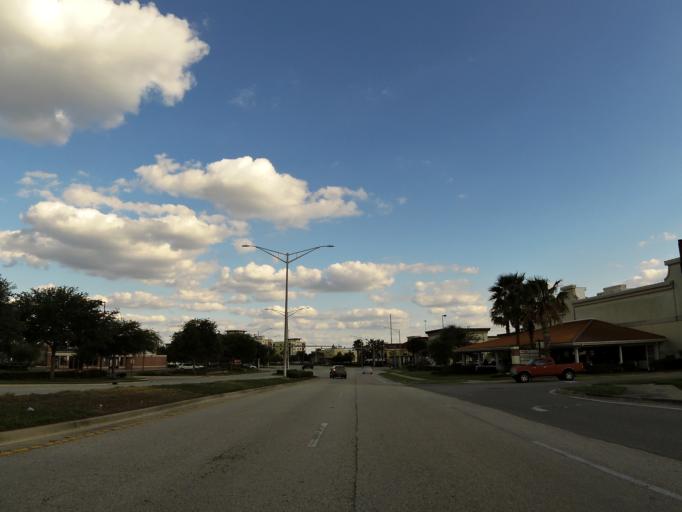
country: US
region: Florida
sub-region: Duval County
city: Jacksonville Beach
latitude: 30.2547
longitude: -81.5303
